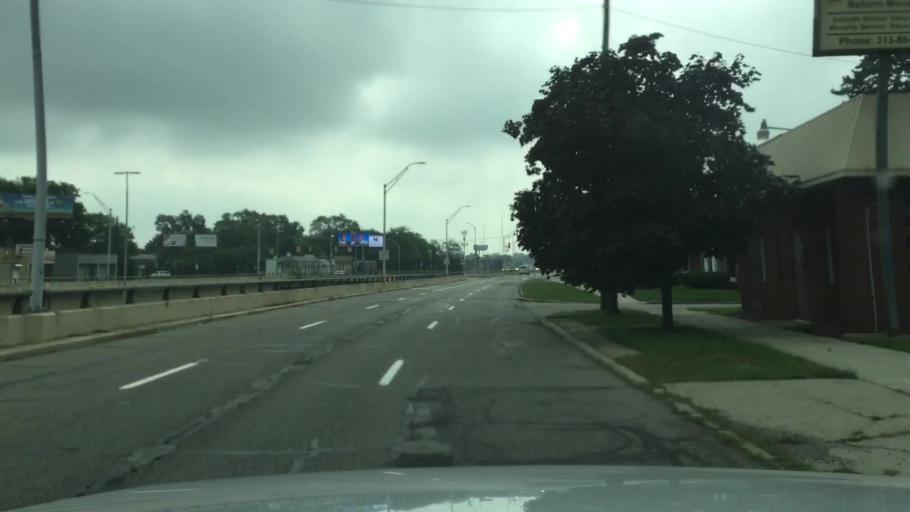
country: US
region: Michigan
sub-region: Oakland County
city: Oak Park
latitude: 42.4107
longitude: -83.1665
